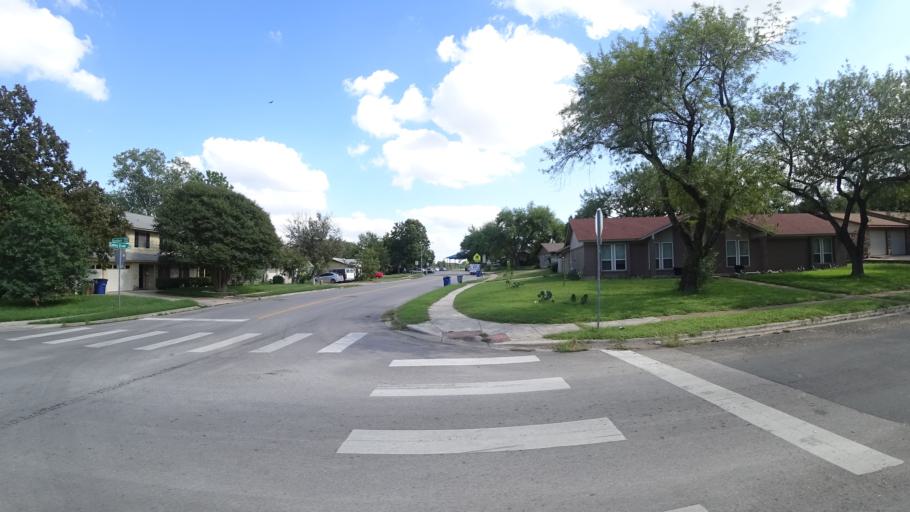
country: US
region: Texas
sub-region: Travis County
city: Wells Branch
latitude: 30.3664
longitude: -97.7114
